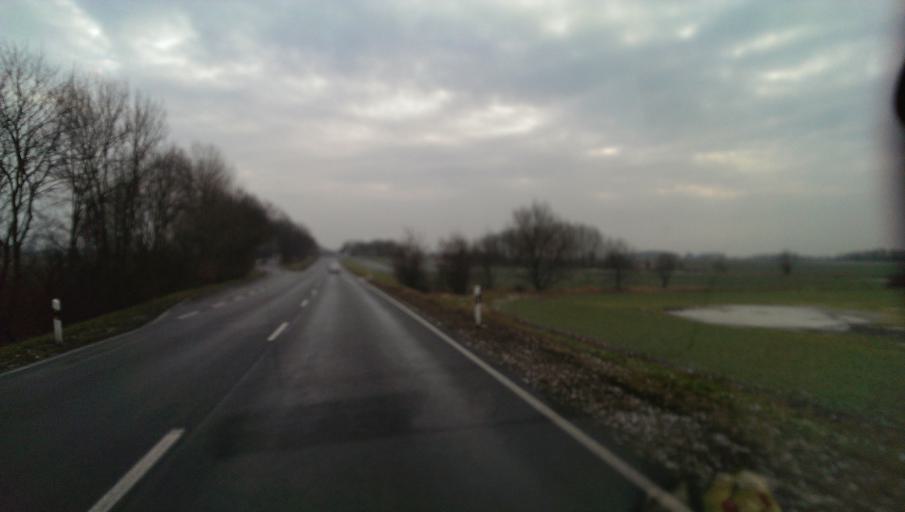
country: DE
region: Saxony
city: Zabeltitz
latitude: 51.3545
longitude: 13.5322
